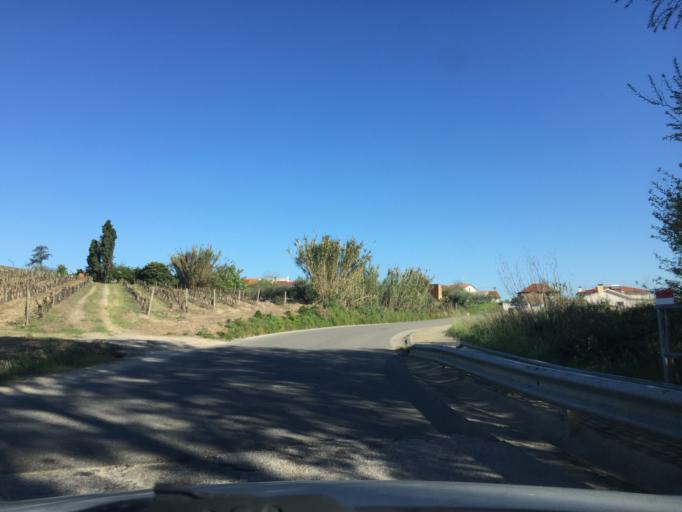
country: PT
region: Aveiro
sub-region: Anadia
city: Sangalhos
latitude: 40.4644
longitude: -8.5010
